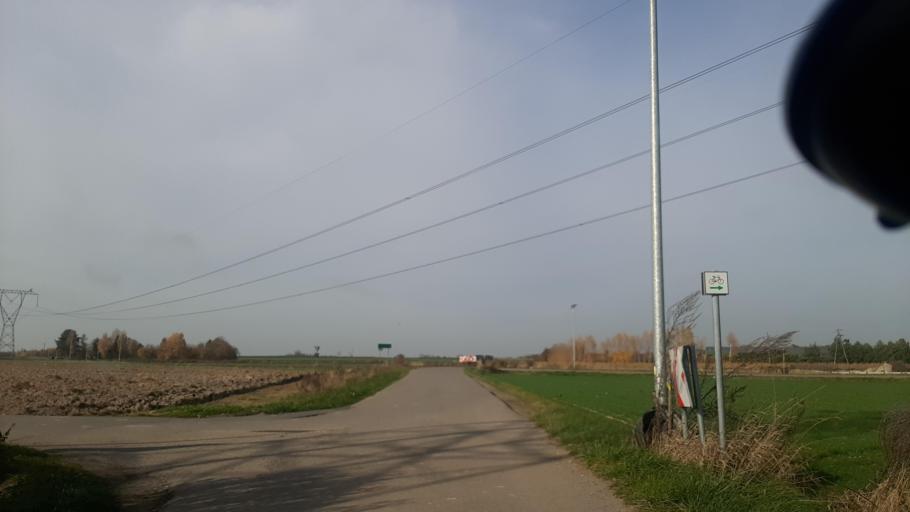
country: PL
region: Lublin Voivodeship
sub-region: Powiat lubelski
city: Lublin
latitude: 51.3324
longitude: 22.5419
